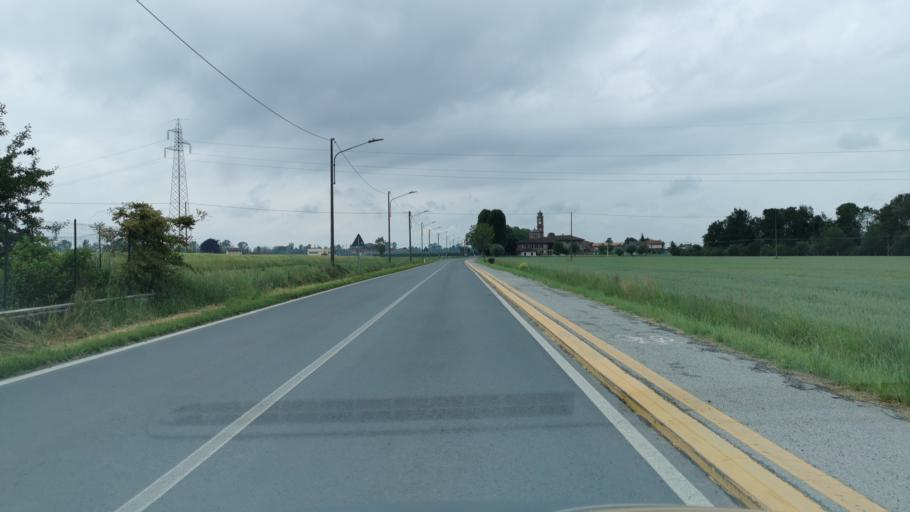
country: IT
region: Piedmont
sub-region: Provincia di Cuneo
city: Savigliano
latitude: 44.6315
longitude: 7.6412
